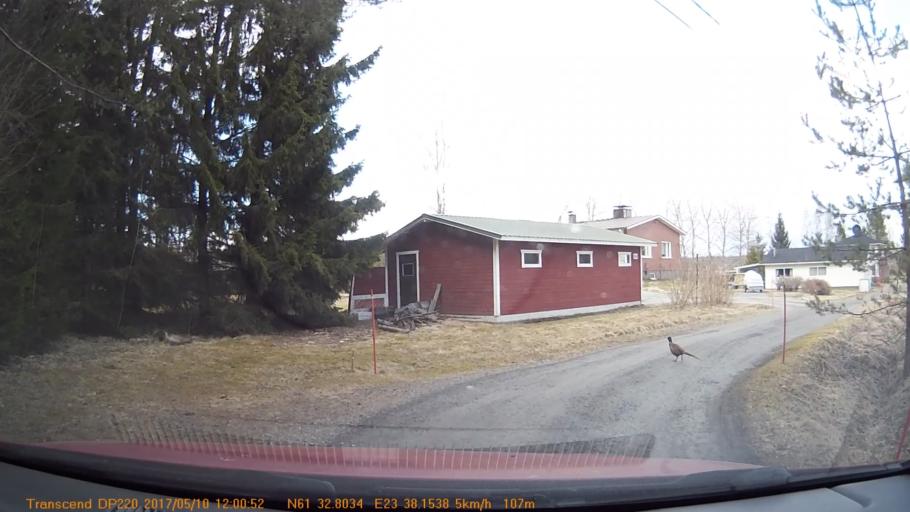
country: FI
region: Pirkanmaa
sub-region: Tampere
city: Yloejaervi
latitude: 61.5469
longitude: 23.6358
